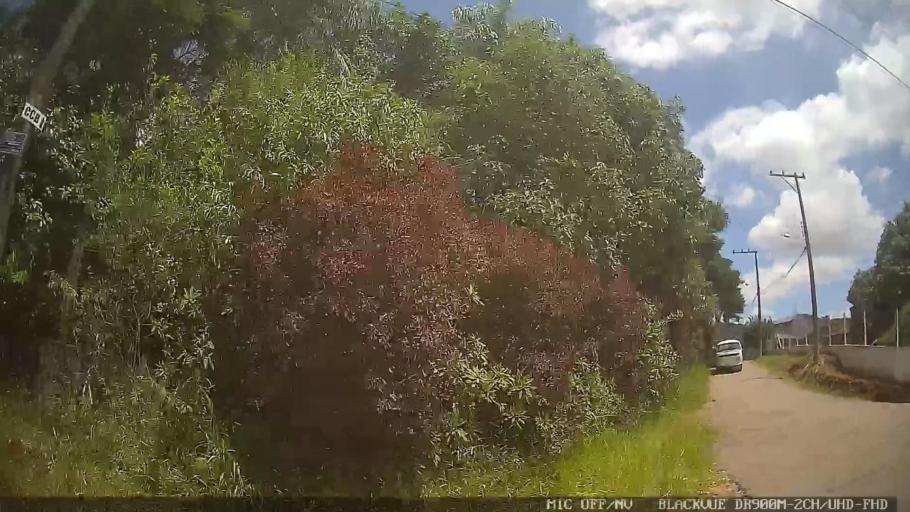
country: BR
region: Sao Paulo
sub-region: Braganca Paulista
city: Braganca Paulista
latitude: -23.0252
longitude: -46.5413
